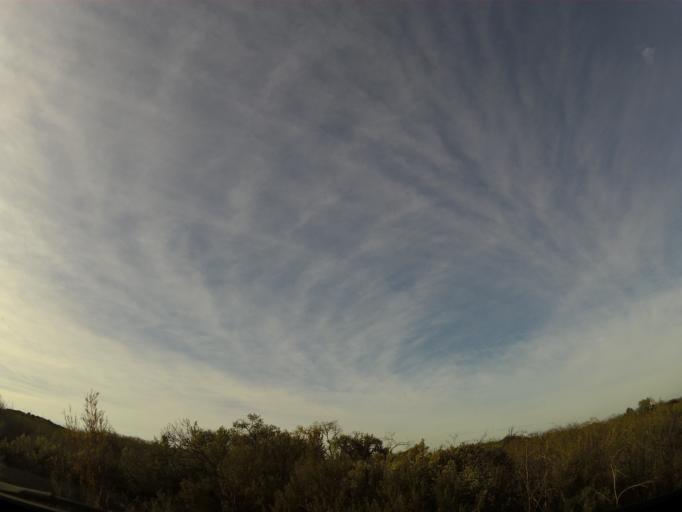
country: US
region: California
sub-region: San Benito County
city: Ridgemark
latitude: 36.8154
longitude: -121.3936
